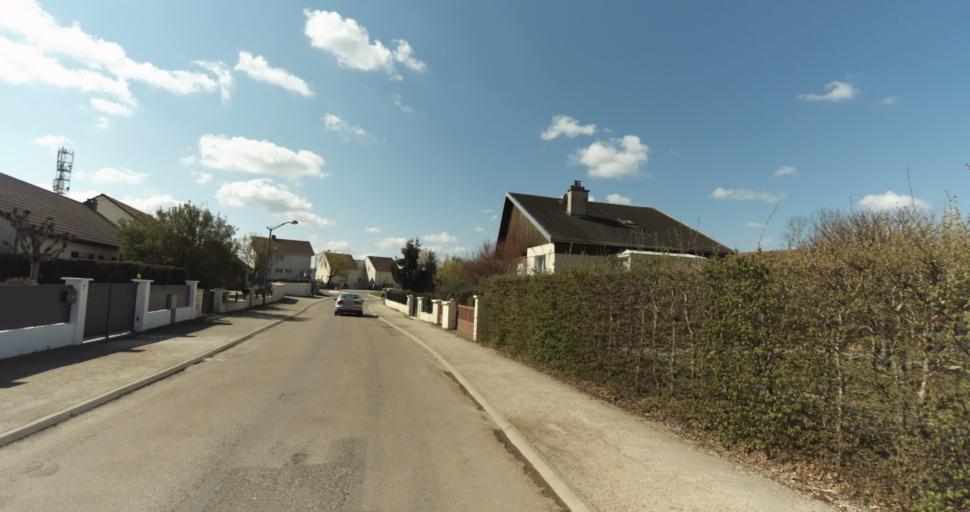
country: FR
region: Bourgogne
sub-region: Departement de la Cote-d'Or
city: Auxonne
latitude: 47.1958
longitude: 5.3949
